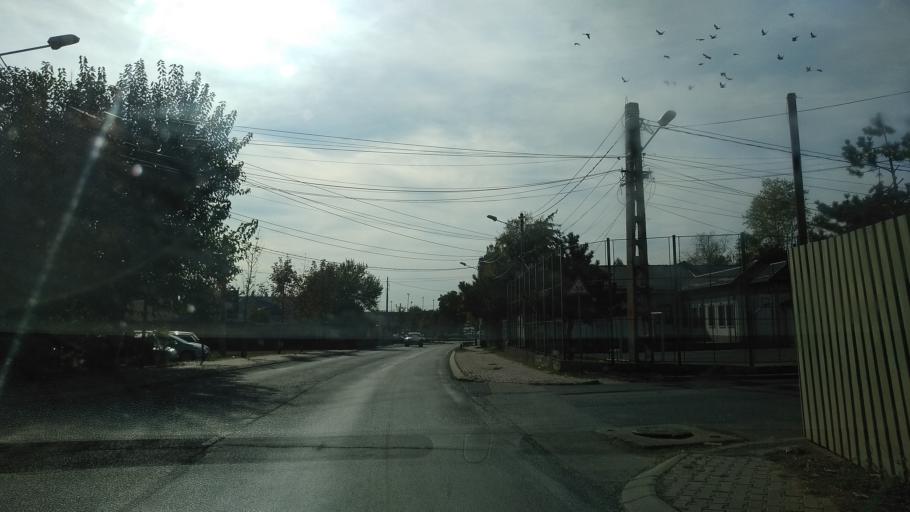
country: RO
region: Ilfov
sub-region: Comuna Chitila
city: Chitila
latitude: 44.5089
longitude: 25.9843
